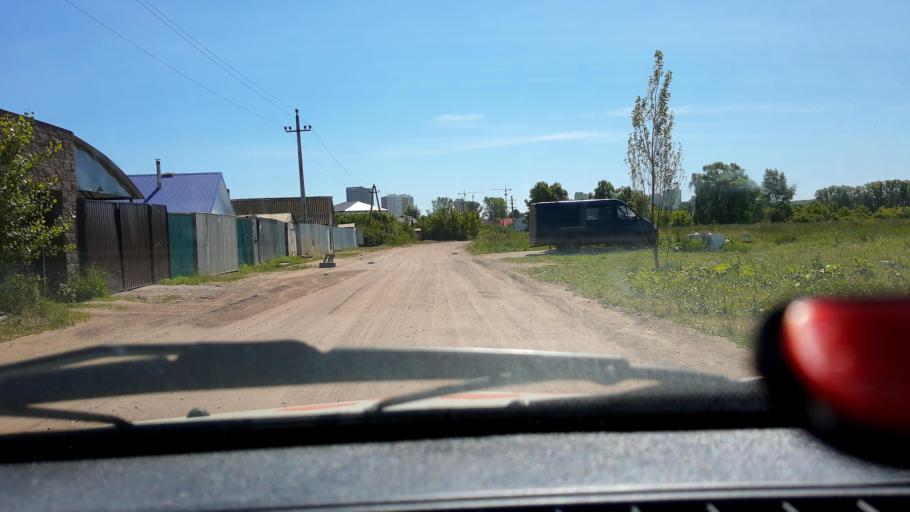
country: RU
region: Bashkortostan
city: Mikhaylovka
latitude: 54.7095
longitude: 55.8672
